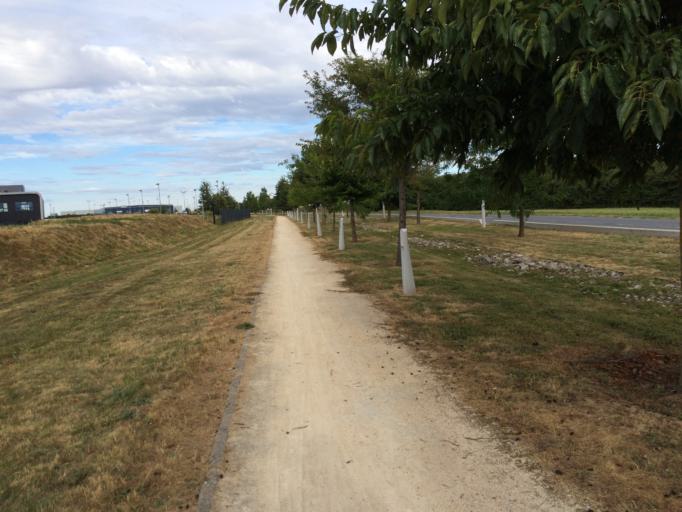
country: FR
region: Ile-de-France
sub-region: Departement de l'Essonne
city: Chilly-Mazarin
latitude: 48.7186
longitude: 2.3302
